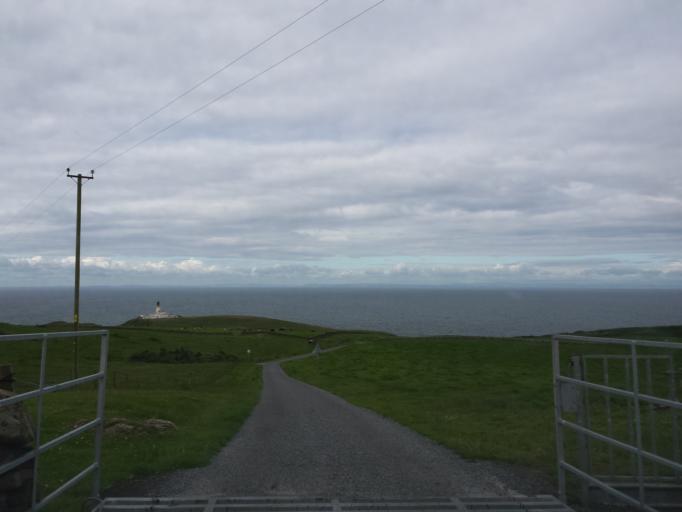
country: GB
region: Scotland
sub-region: Dumfries and Galloway
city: Stranraer
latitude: 54.8662
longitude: -5.1351
